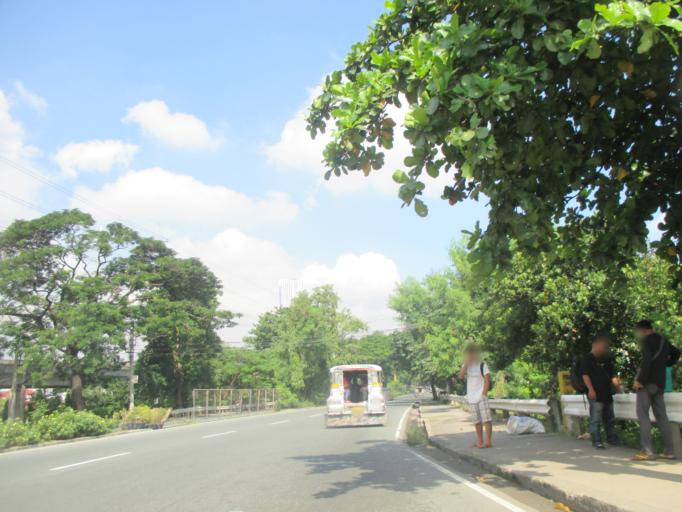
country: PH
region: Metro Manila
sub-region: Marikina
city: Calumpang
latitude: 14.6275
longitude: 121.0814
